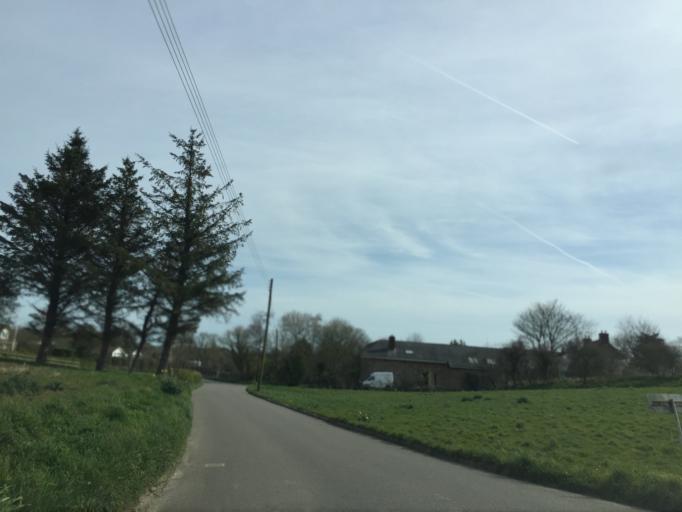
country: JE
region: St Helier
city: Saint Helier
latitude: 49.2306
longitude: -2.1046
